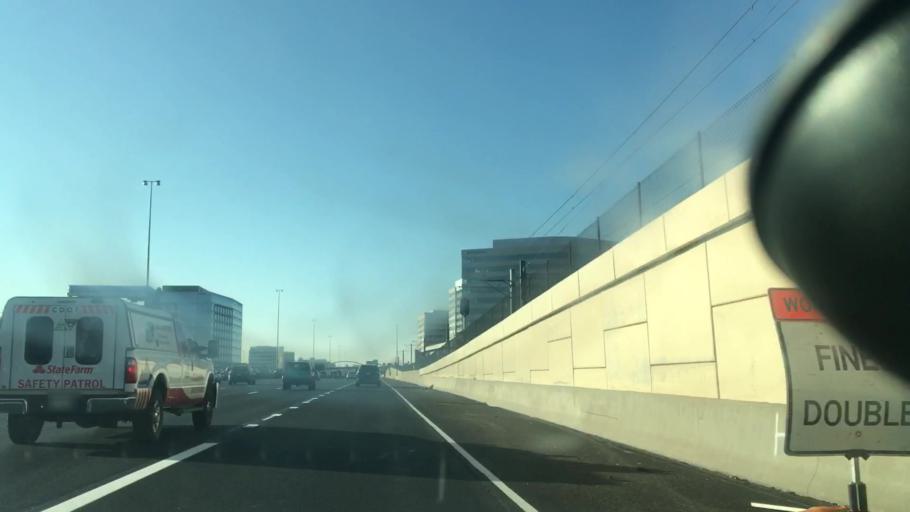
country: US
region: Colorado
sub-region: Arapahoe County
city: Castlewood
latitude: 39.6068
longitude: -104.8902
